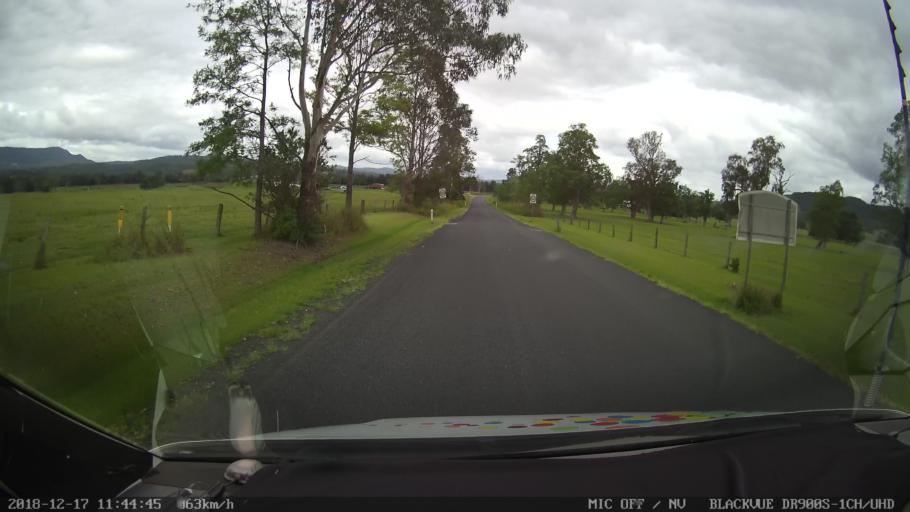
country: AU
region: New South Wales
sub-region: Kyogle
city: Kyogle
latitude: -28.6504
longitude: 152.5951
